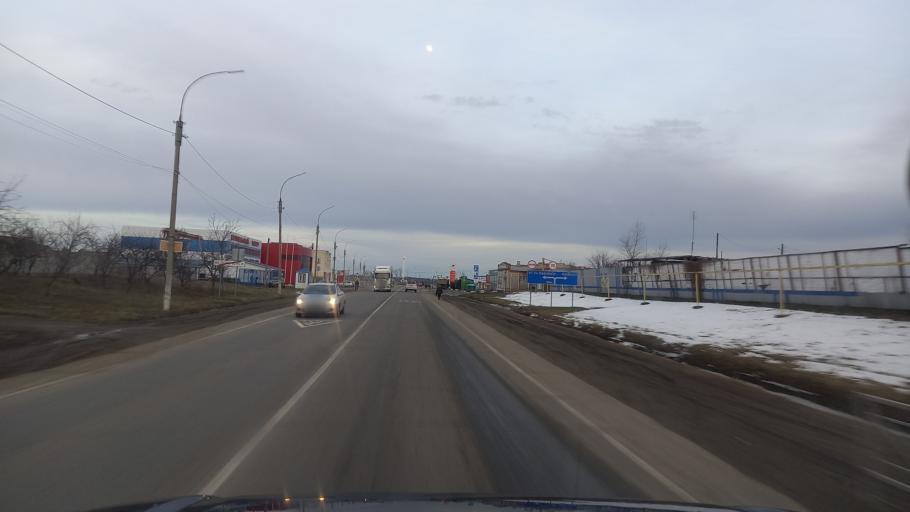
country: RU
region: Krasnodarskiy
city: Belorechensk
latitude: 44.7728
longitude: 39.9022
